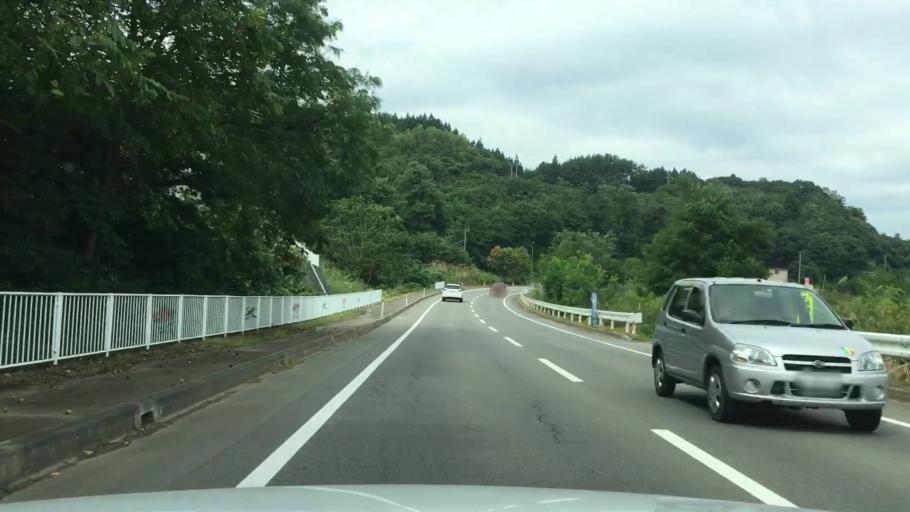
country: JP
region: Aomori
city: Shimokizukuri
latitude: 40.7614
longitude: 140.2269
